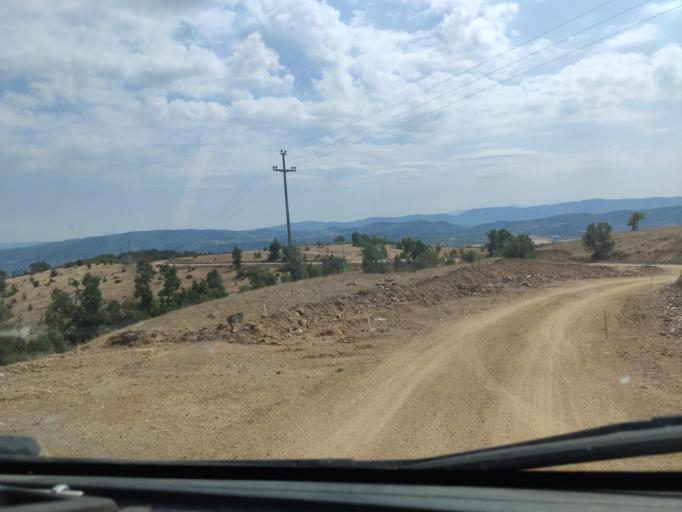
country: MK
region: Radovis
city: Radovish
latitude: 41.6699
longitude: 22.4053
